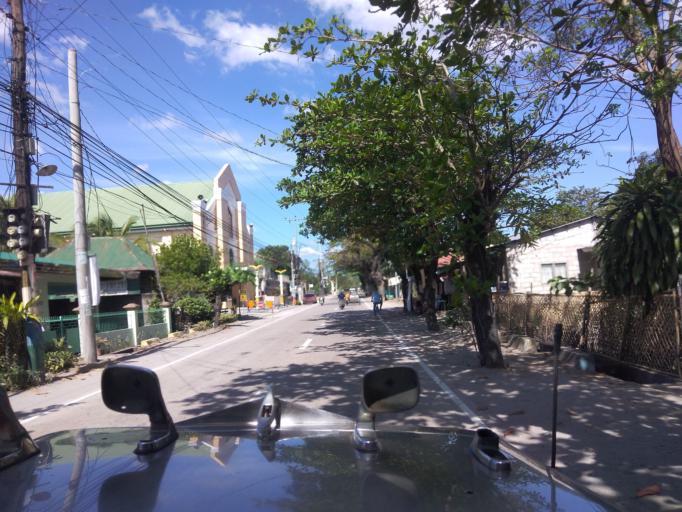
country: PH
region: Central Luzon
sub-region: Province of Pampanga
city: Santa Rita
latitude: 15.0016
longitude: 120.6093
